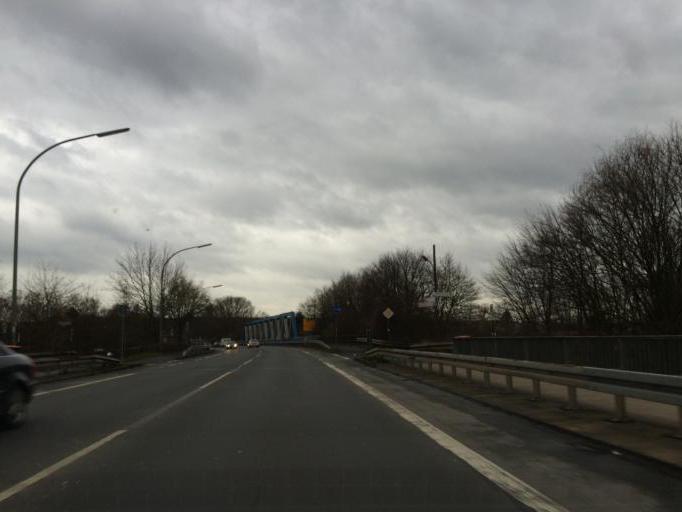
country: DE
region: North Rhine-Westphalia
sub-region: Regierungsbezirk Munster
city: Haltern
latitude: 51.7304
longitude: 7.1865
